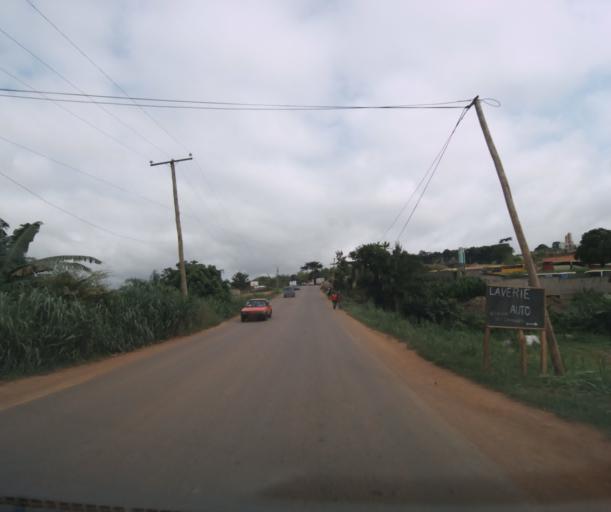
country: CM
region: Centre
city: Yaounde
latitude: 3.8064
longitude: 11.5200
